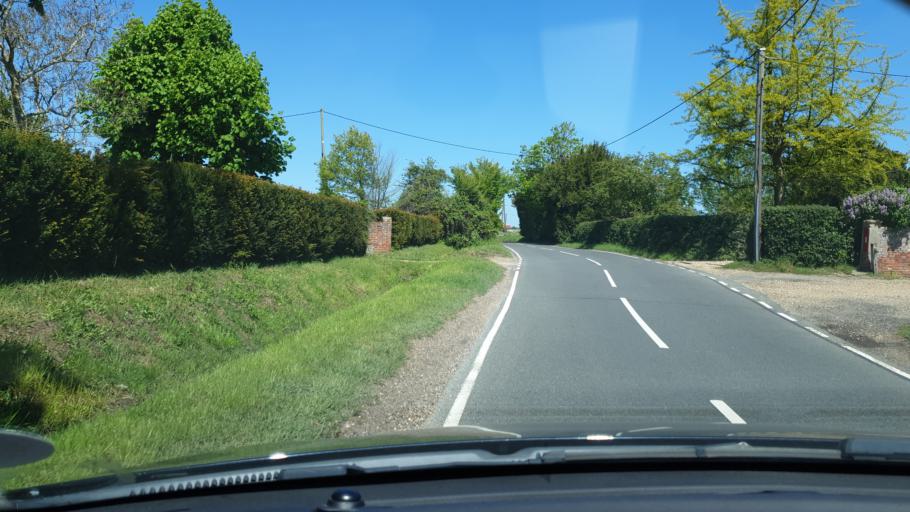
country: GB
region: England
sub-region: Essex
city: Little Clacton
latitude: 51.8719
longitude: 1.1241
